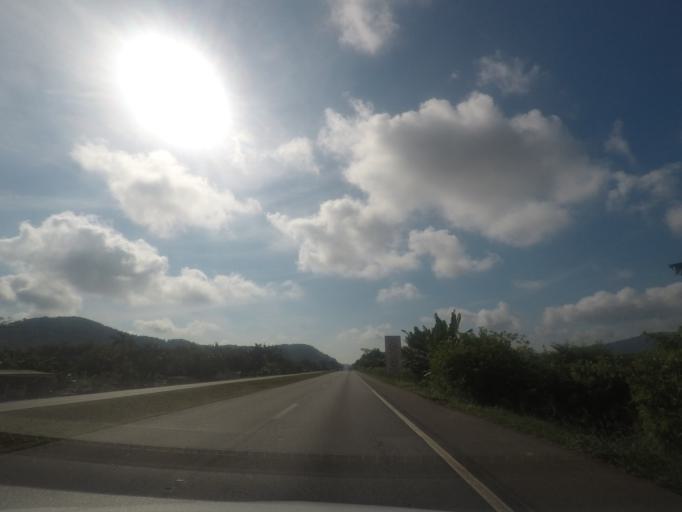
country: BR
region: Parana
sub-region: Antonina
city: Antonina
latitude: -25.5385
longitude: -48.7715
